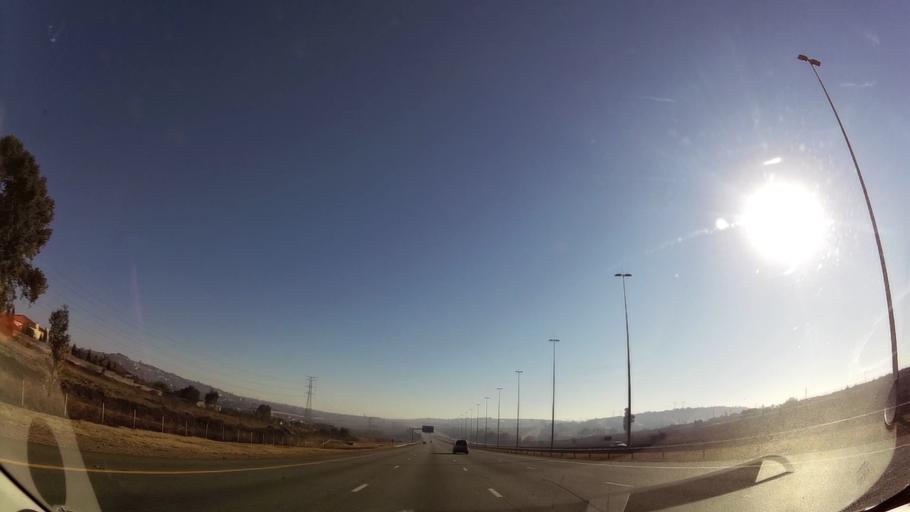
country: ZA
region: Gauteng
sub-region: City of Tshwane Metropolitan Municipality
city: Centurion
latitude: -25.8847
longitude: 28.2548
